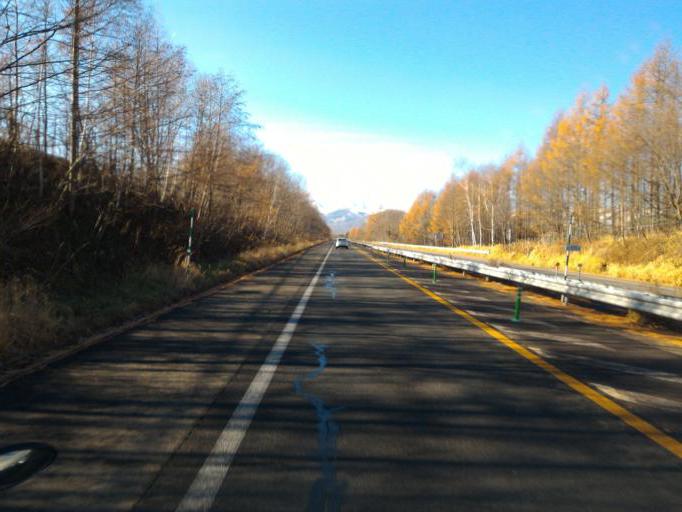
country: JP
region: Hokkaido
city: Otofuke
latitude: 42.9746
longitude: 142.9137
